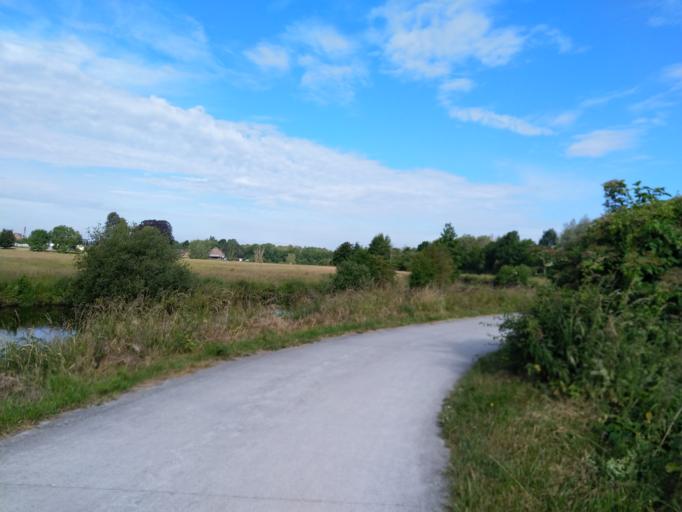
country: FR
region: Nord-Pas-de-Calais
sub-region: Departement du Nord
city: Boussois
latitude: 50.2848
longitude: 4.0537
